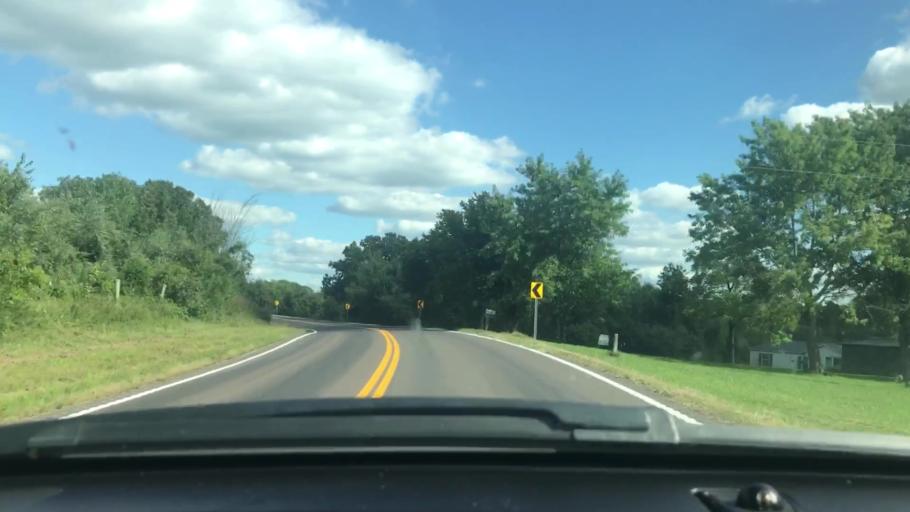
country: US
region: Missouri
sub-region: Wright County
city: Mountain Grove
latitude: 37.2549
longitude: -92.3068
